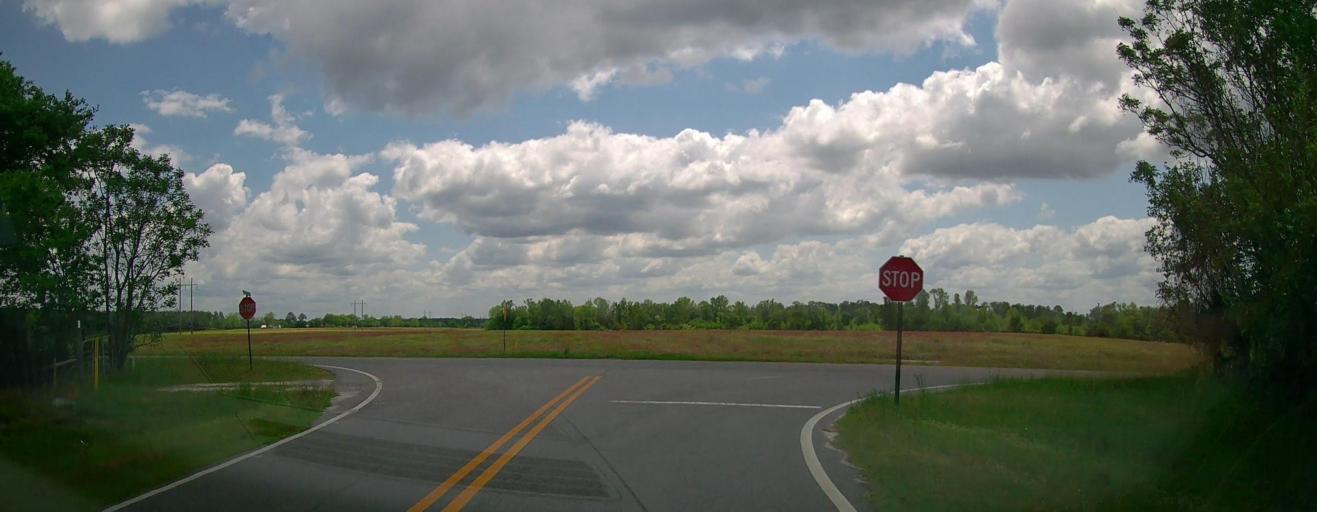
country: US
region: Georgia
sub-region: Laurens County
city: Dublin
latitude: 32.5943
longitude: -82.9301
